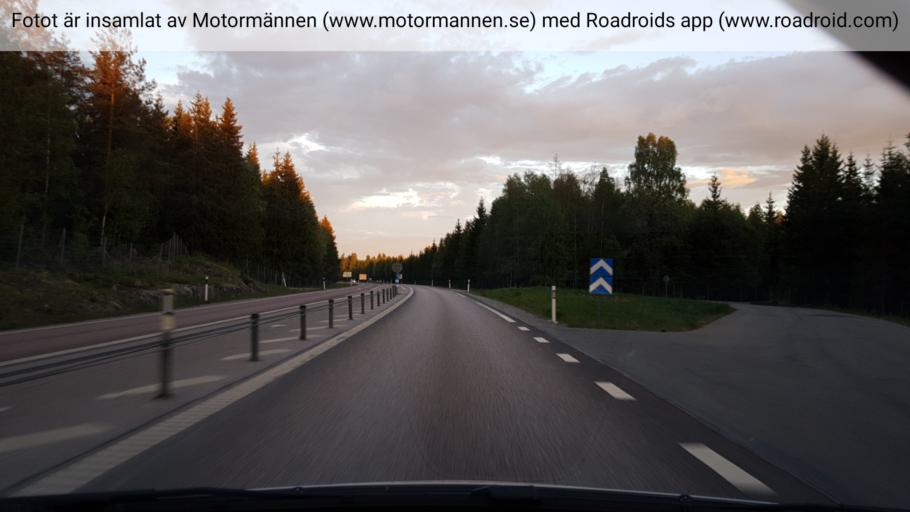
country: SE
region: Vaestmanland
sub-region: Norbergs Kommun
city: Norberg
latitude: 59.8794
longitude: 16.0170
